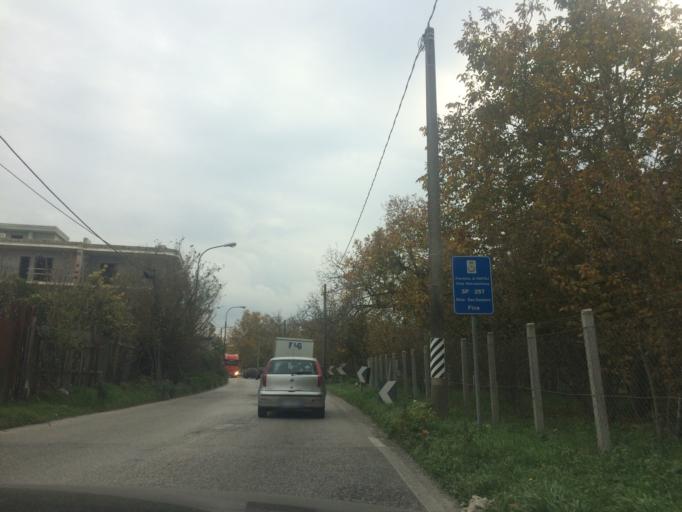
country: IT
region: Campania
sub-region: Provincia di Napoli
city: Piazzolla
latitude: 40.8855
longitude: 14.5304
